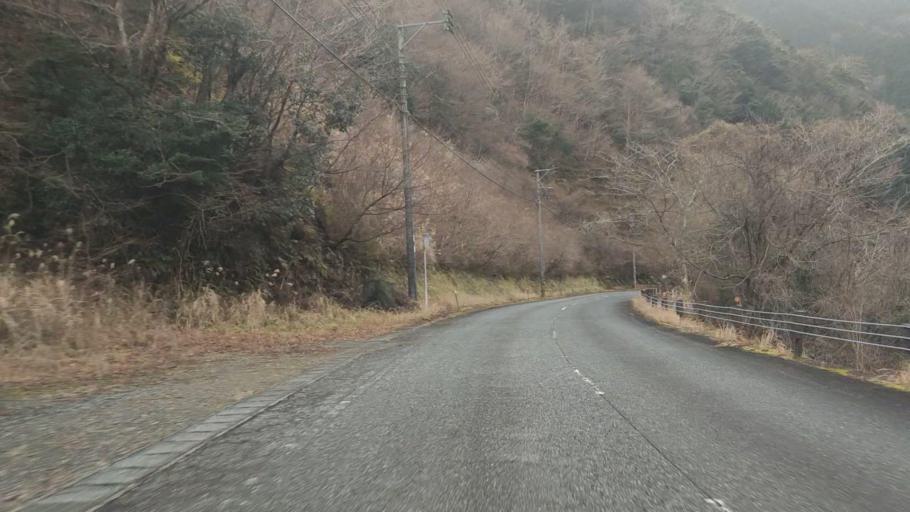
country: JP
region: Kumamoto
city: Matsubase
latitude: 32.5104
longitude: 130.9248
